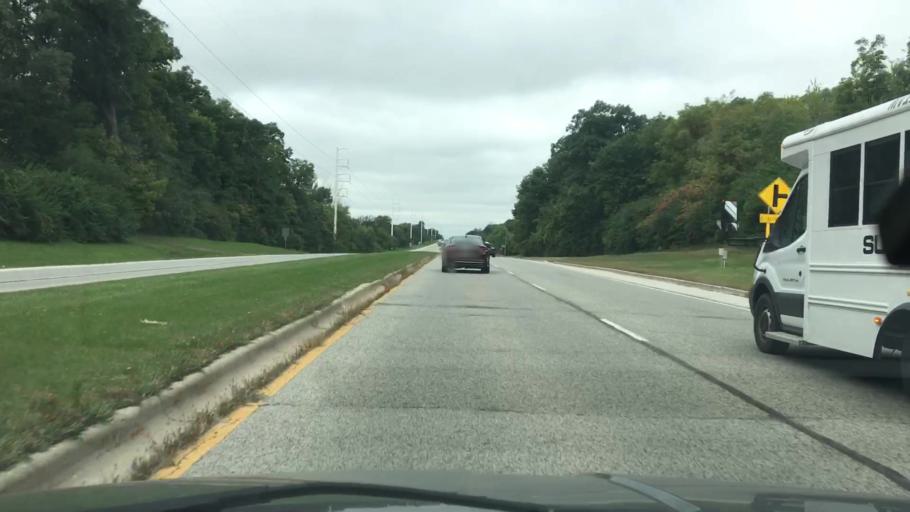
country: US
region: Illinois
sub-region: DuPage County
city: Woodridge
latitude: 41.7494
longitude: -88.0857
